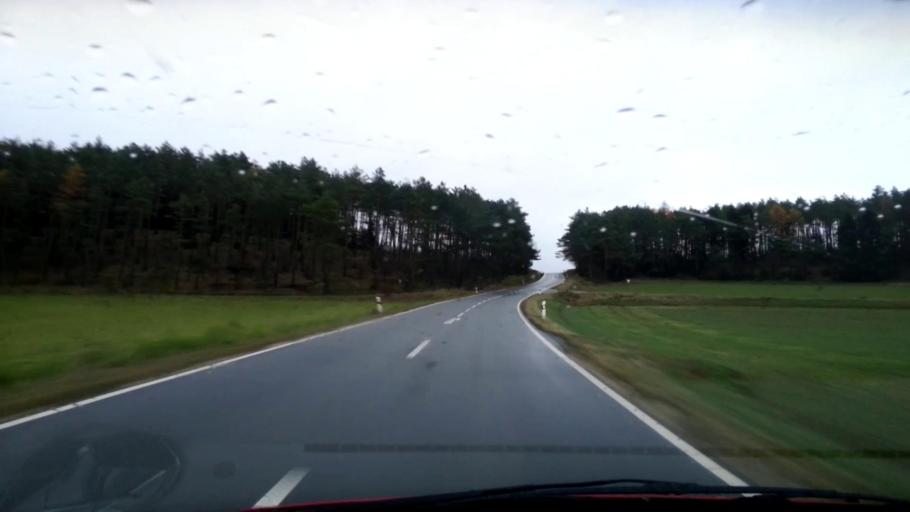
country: DE
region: Bavaria
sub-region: Upper Franconia
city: Aufsess
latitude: 49.9392
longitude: 11.2108
